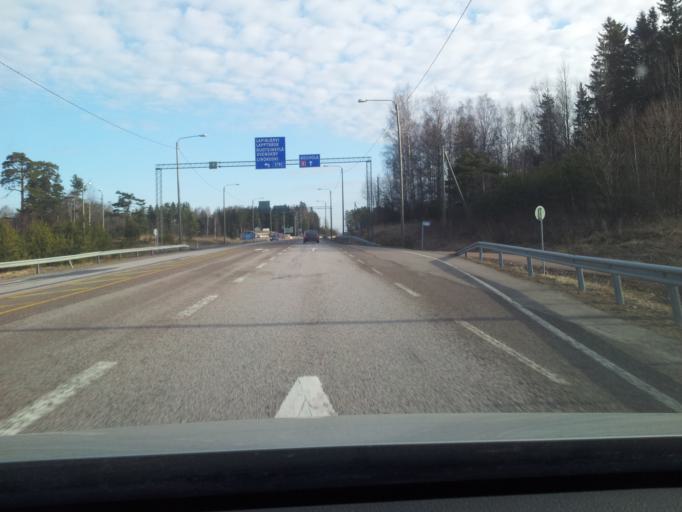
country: FI
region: Uusimaa
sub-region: Loviisa
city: Lapinjaervi
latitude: 60.6353
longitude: 26.2277
